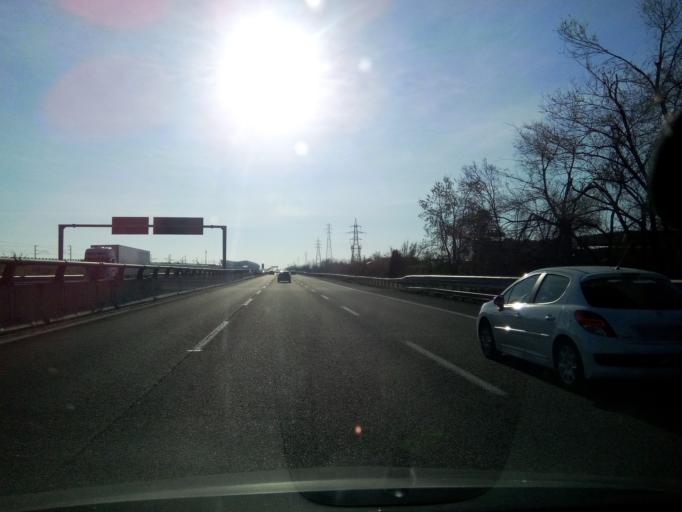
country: IT
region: Emilia-Romagna
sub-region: Provincia di Reggio Emilia
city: Reggio nell'Emilia
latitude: 44.7267
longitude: 10.6398
